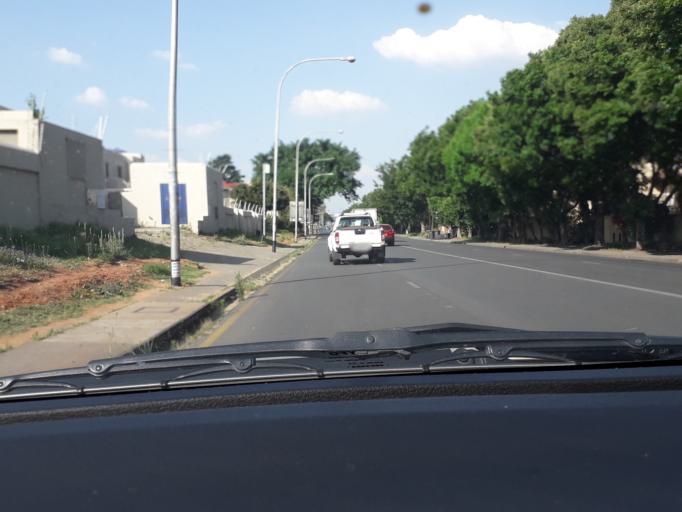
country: ZA
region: Gauteng
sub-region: City of Johannesburg Metropolitan Municipality
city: Modderfontein
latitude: -26.1302
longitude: 28.1010
